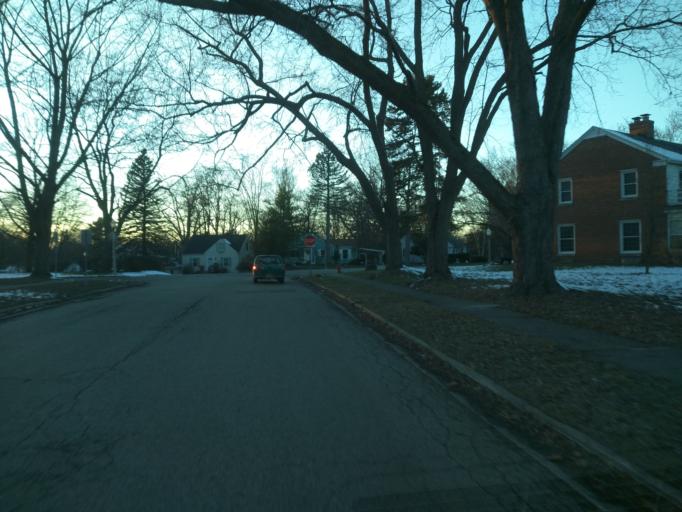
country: US
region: Michigan
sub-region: Ingham County
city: Lansing
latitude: 42.6987
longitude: -84.5423
